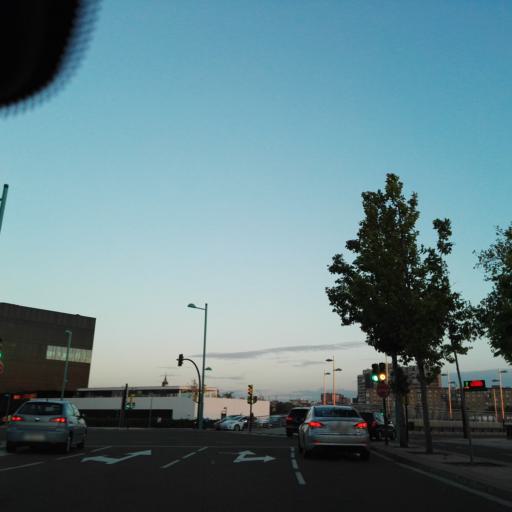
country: ES
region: Aragon
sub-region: Provincia de Zaragoza
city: Almozara
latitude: 41.6627
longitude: -0.8896
